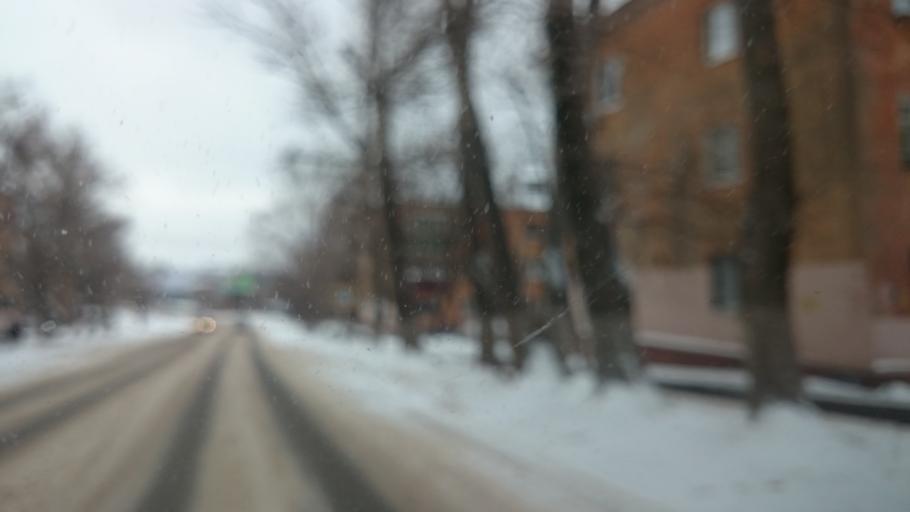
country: RU
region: Tula
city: Tula
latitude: 54.1892
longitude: 37.5713
